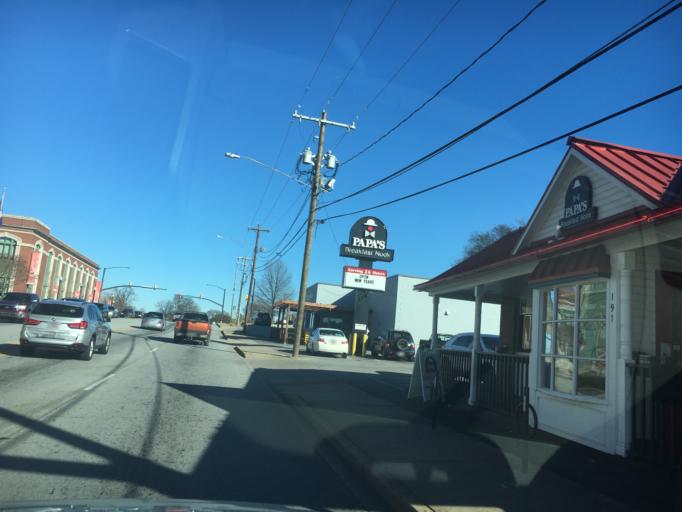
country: US
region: South Carolina
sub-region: Spartanburg County
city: Spartanburg
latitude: 34.9524
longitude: -81.9302
